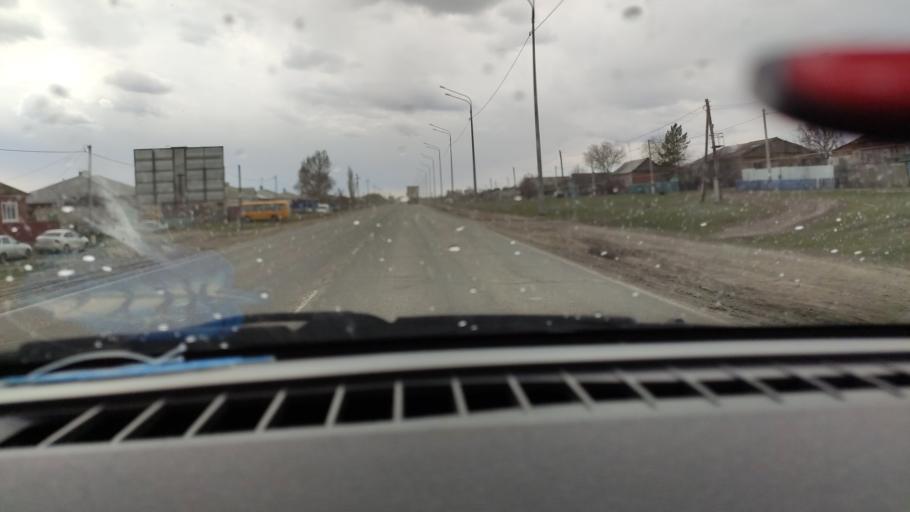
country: RU
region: Saratov
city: Sinodskoye
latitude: 51.9920
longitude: 46.6695
